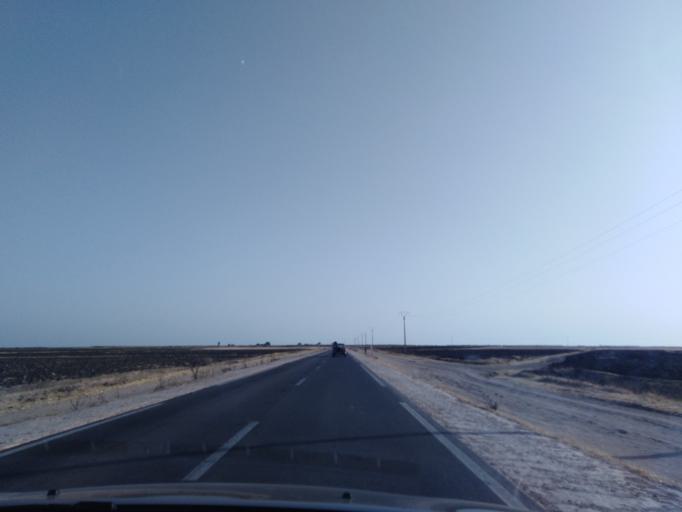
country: MA
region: Doukkala-Abda
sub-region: El-Jadida
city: Sidi Bennour
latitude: 32.5332
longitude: -8.7321
